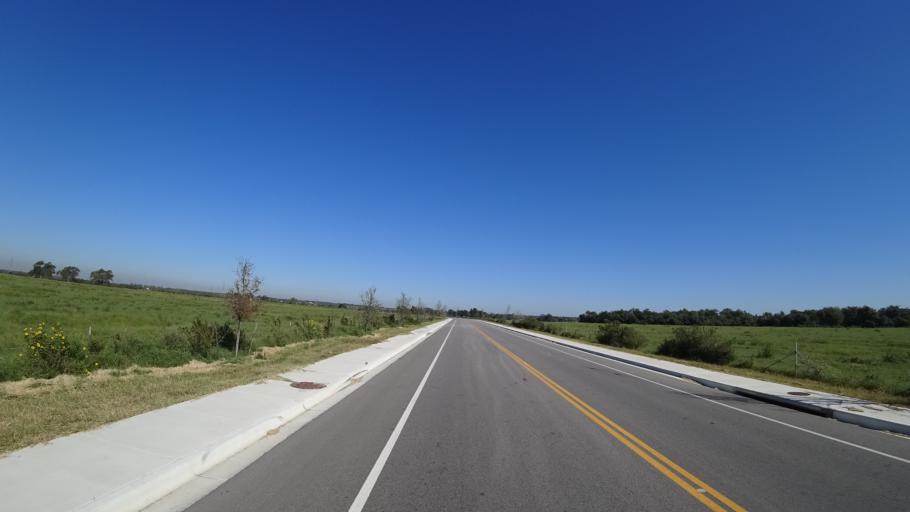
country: US
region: Texas
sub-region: Travis County
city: Hornsby Bend
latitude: 30.2444
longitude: -97.5932
